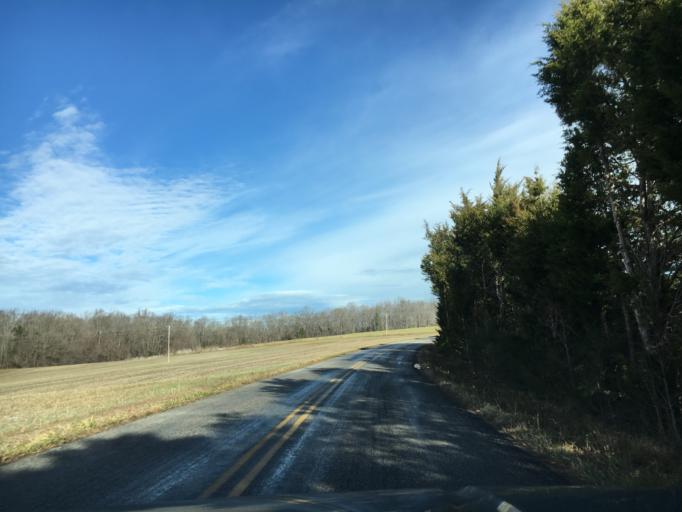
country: US
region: Virginia
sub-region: Nottoway County
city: Crewe
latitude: 37.3208
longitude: -78.1744
